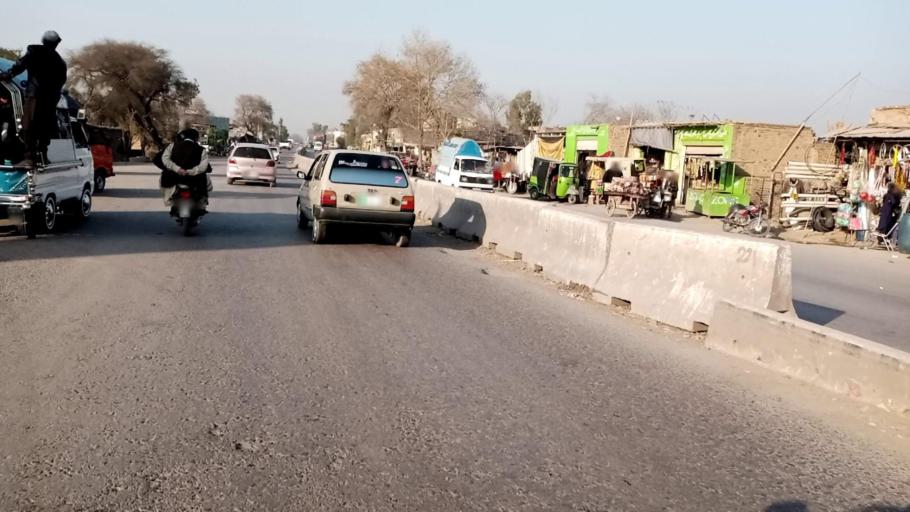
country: PK
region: Khyber Pakhtunkhwa
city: Peshawar
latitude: 33.9392
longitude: 71.5554
